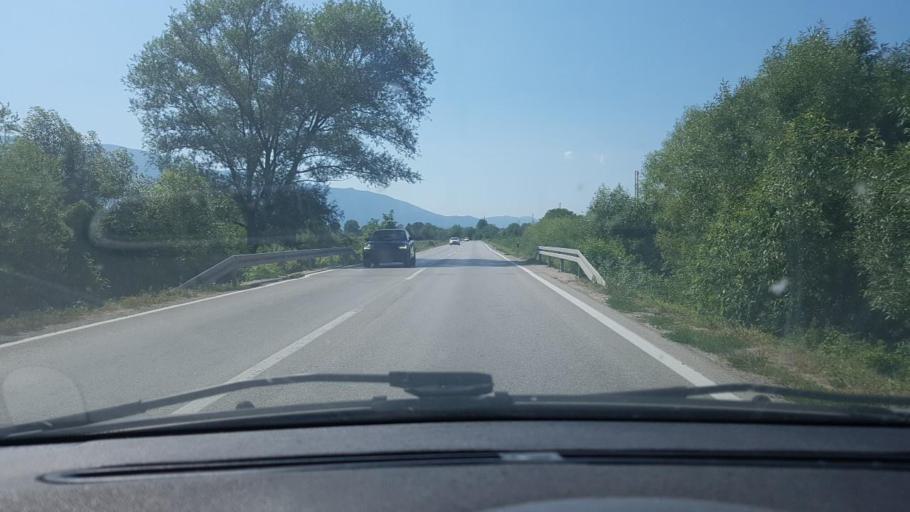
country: BA
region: Federation of Bosnia and Herzegovina
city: Bihac
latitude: 44.8055
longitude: 15.8972
